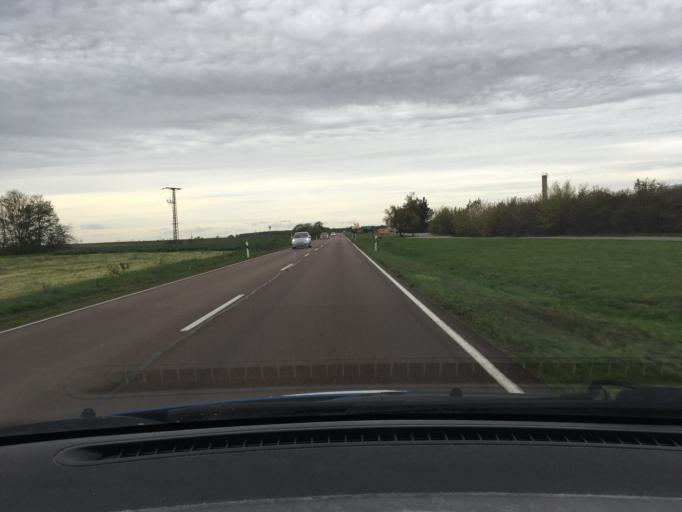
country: DE
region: Saxony-Anhalt
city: Leitzkau
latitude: 52.0180
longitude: 12.0097
